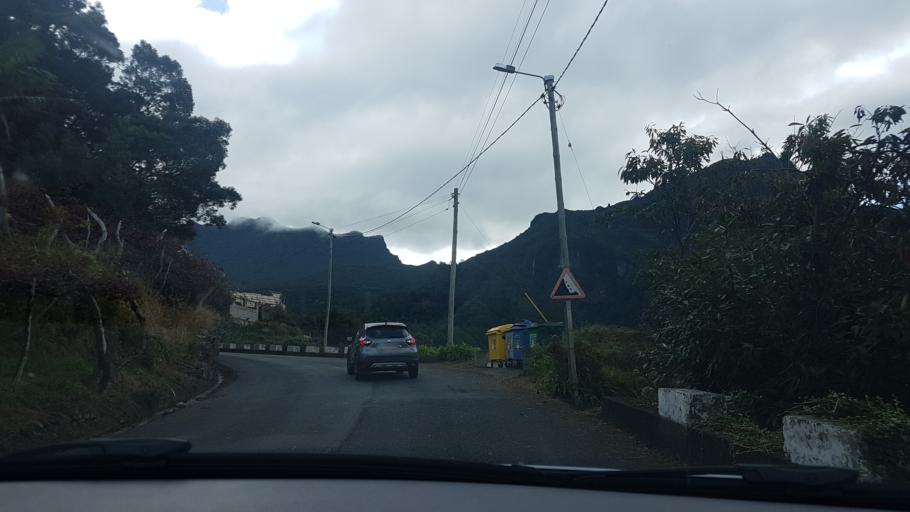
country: PT
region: Madeira
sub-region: Sao Vicente
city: Sao Vicente
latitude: 32.7778
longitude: -17.0290
